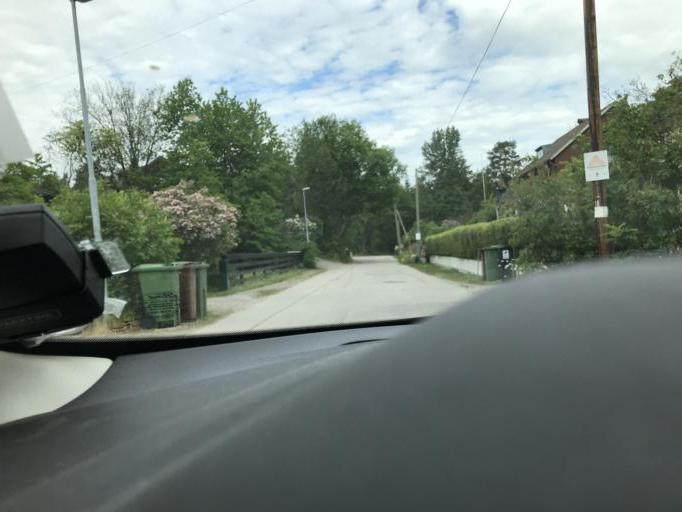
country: SE
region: Stockholm
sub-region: Botkyrka Kommun
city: Tumba
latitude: 59.1974
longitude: 17.8184
